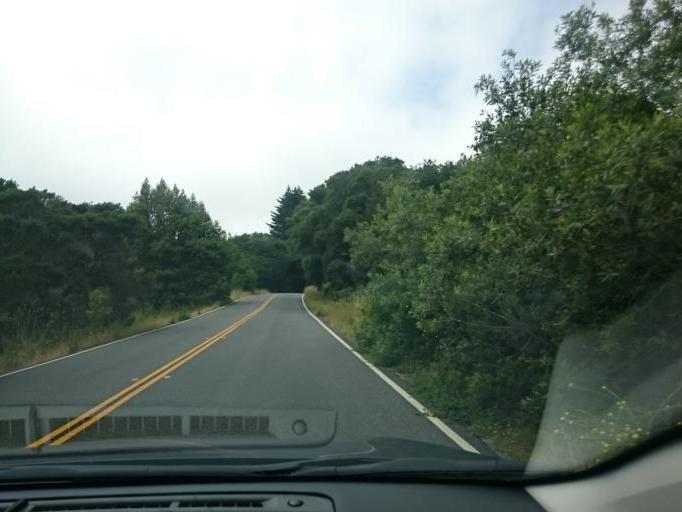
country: US
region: California
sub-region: Marin County
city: Lagunitas-Forest Knolls
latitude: 37.9807
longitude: -122.7384
